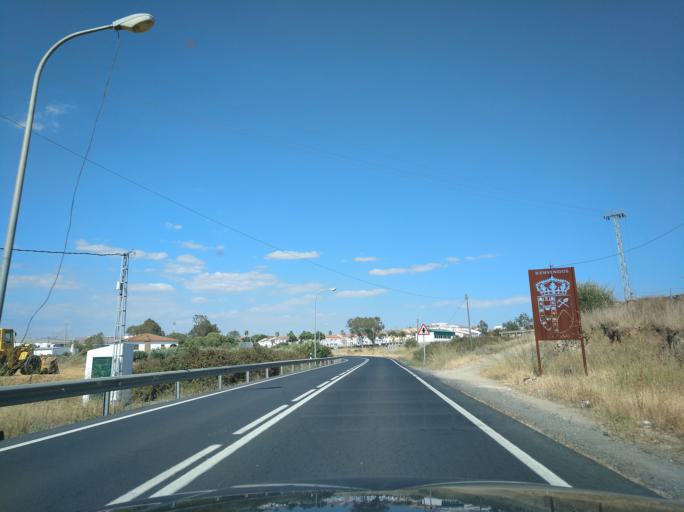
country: ES
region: Andalusia
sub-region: Provincia de Huelva
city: Alosno
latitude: 37.5464
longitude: -7.1227
